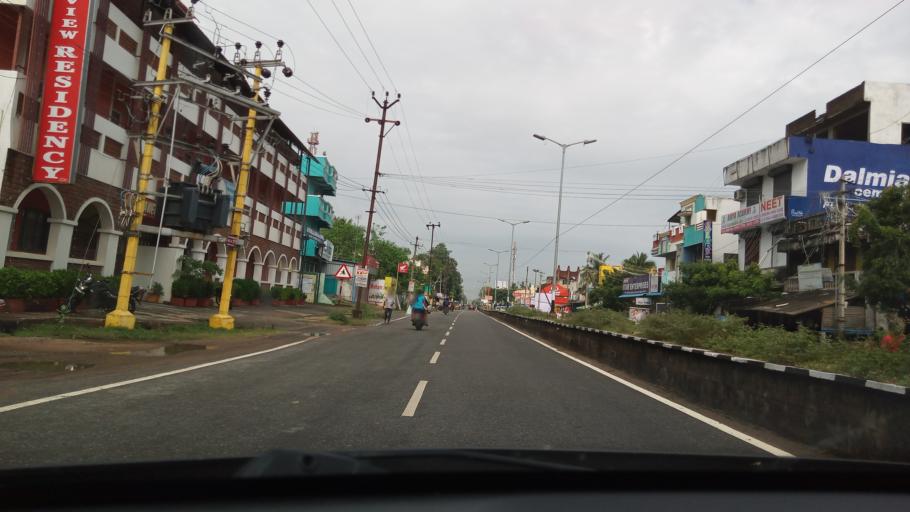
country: IN
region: Tamil Nadu
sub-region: Villupuram
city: Auroville
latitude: 12.0282
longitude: 79.8628
